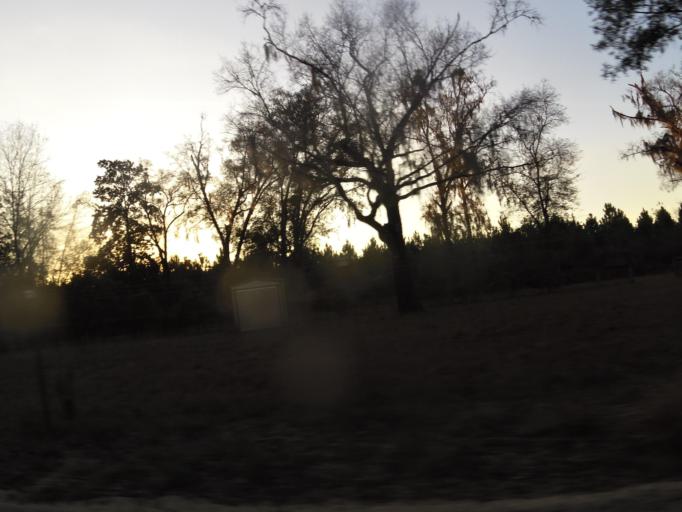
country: US
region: Florida
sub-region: Clay County
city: Green Cove Springs
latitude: 29.8701
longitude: -81.7962
